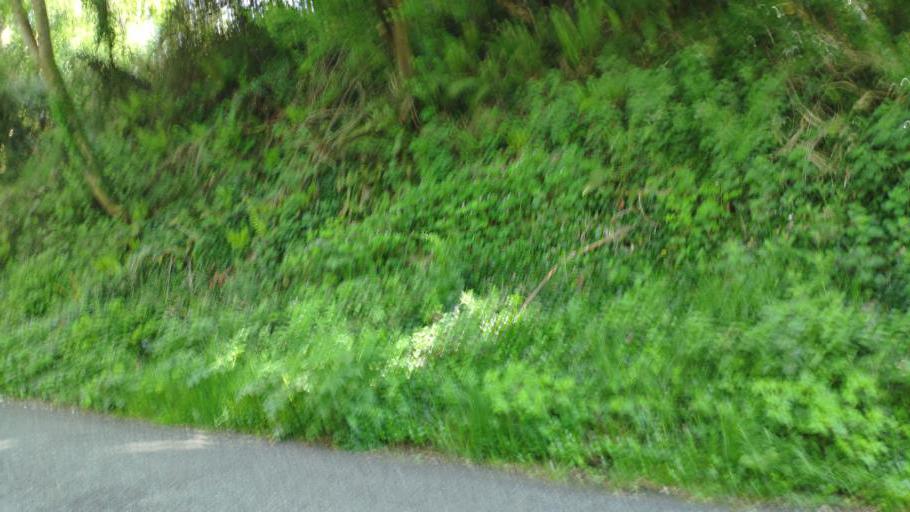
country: IE
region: Munster
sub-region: County Cork
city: Blarney
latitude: 51.9604
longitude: -8.5766
